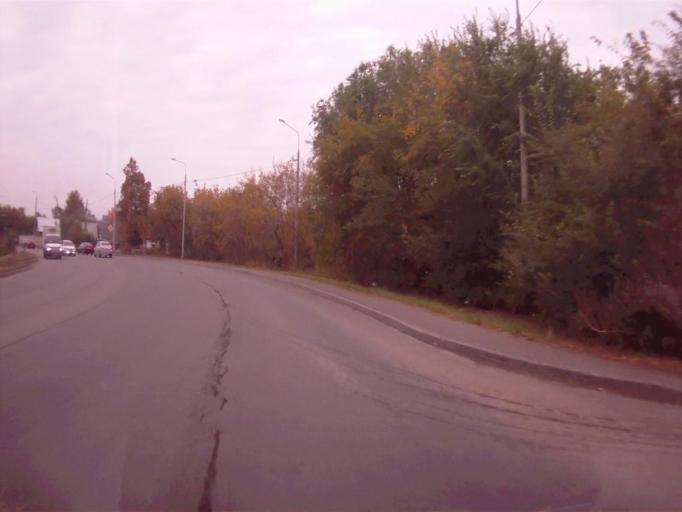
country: RU
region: Chelyabinsk
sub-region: Gorod Chelyabinsk
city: Chelyabinsk
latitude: 55.1334
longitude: 61.3853
